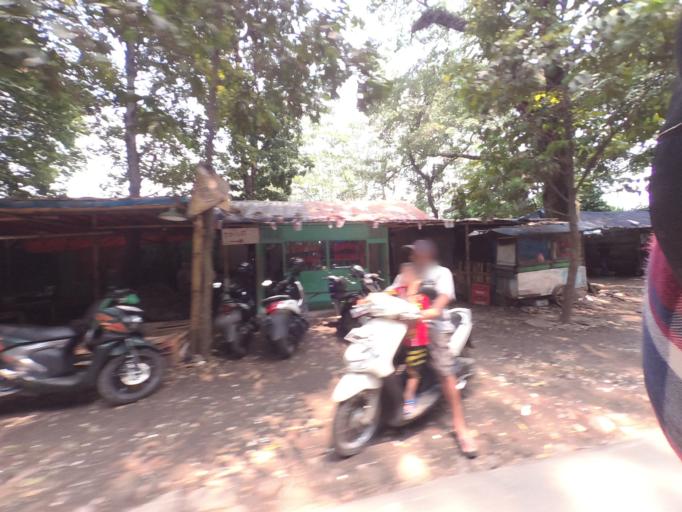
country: ID
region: West Java
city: Bogor
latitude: -6.5704
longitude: 106.7559
